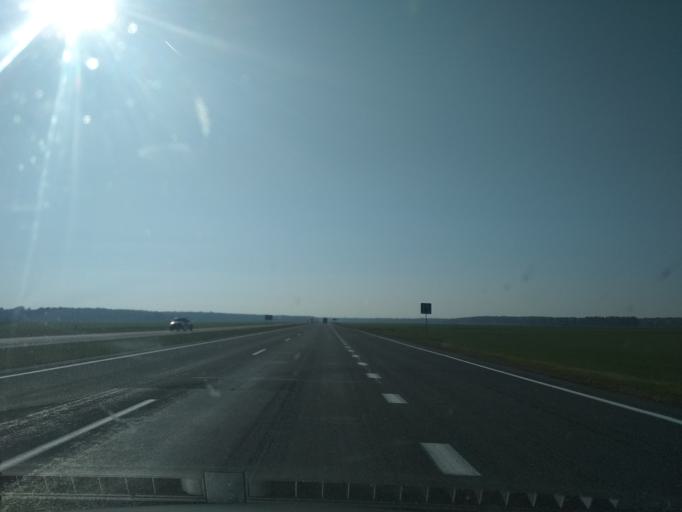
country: BY
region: Brest
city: Antopal'
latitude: 52.3042
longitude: 24.5925
